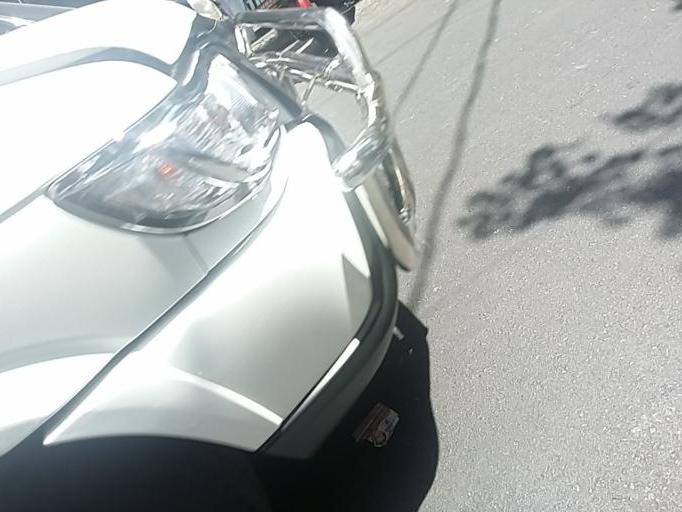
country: PH
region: Metro Manila
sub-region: City of Manila
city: Quiapo
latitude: 14.6007
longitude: 120.9858
